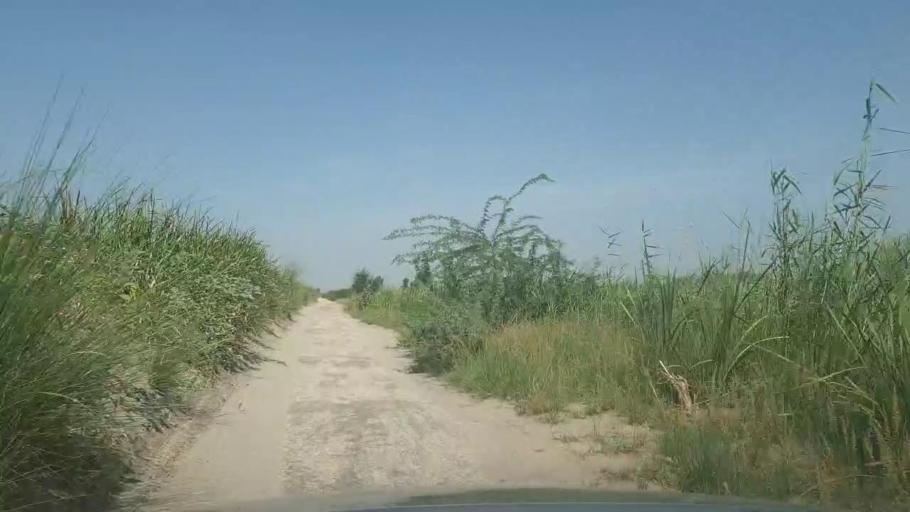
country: PK
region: Sindh
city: Khairpur
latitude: 27.3982
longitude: 69.0641
